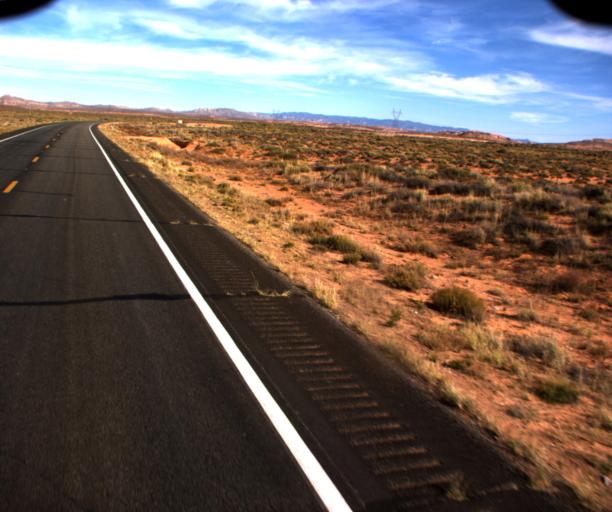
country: US
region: Arizona
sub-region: Apache County
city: Many Farms
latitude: 36.9415
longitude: -109.6529
